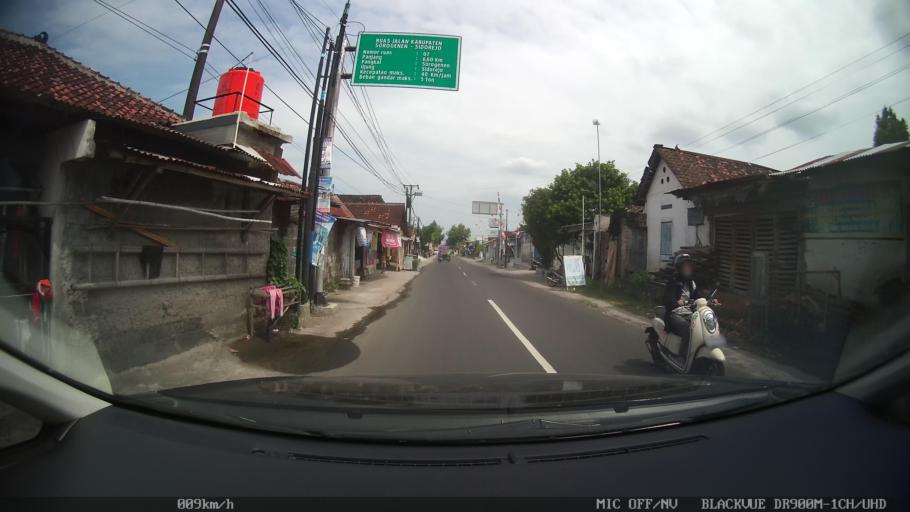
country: ID
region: Daerah Istimewa Yogyakarta
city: Depok
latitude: -7.7299
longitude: 110.4513
